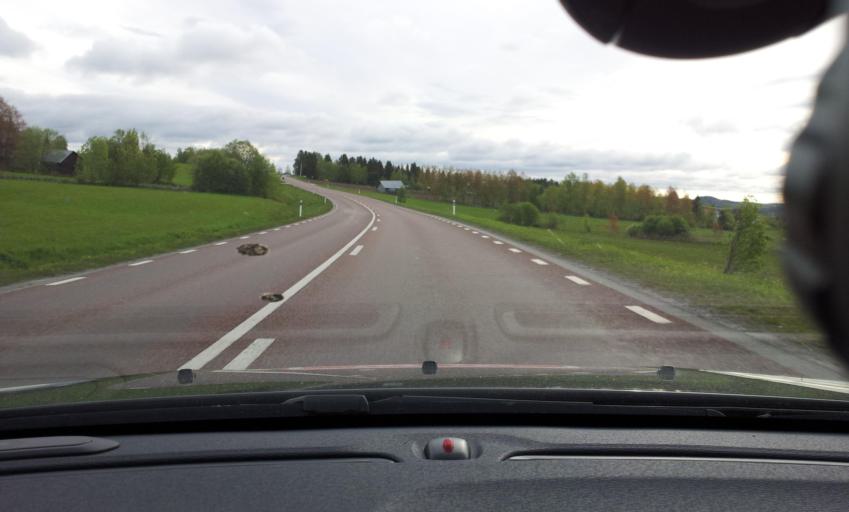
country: SE
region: Jaemtland
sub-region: OEstersunds Kommun
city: Brunflo
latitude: 63.0307
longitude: 14.7911
